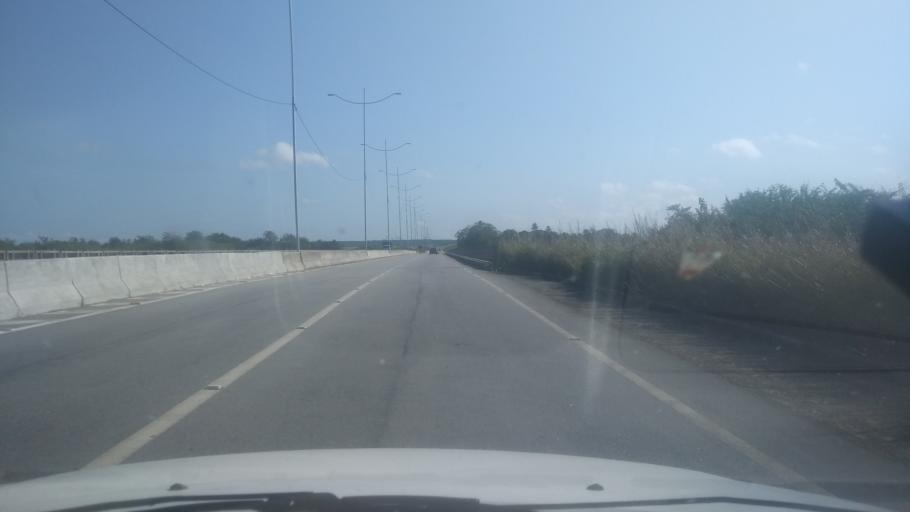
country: BR
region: Rio Grande do Norte
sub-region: Sao Goncalo Do Amarante
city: Sao Goncalo do Amarante
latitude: -5.8111
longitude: -35.3613
